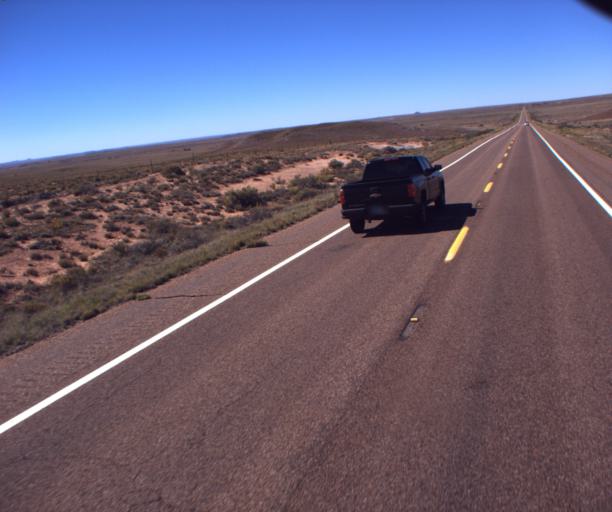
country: US
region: Arizona
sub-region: Navajo County
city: Holbrook
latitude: 34.7790
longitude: -109.8422
